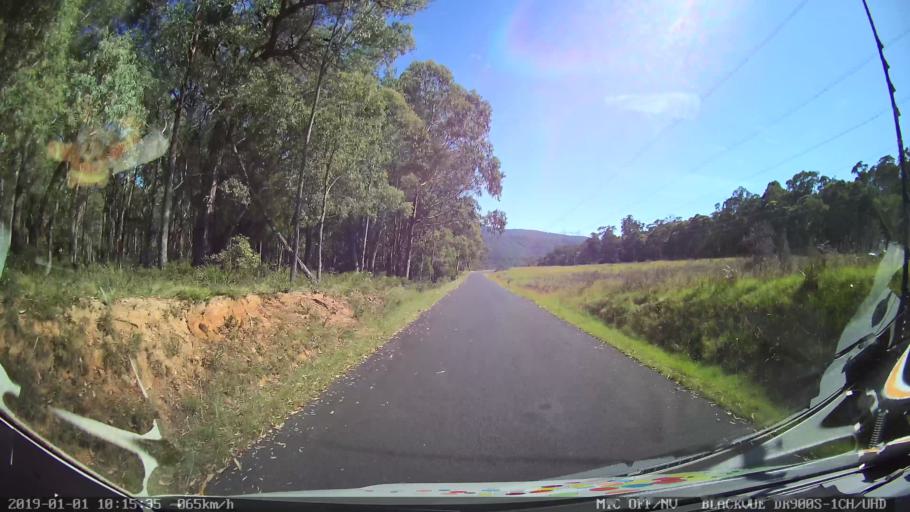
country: AU
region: New South Wales
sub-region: Snowy River
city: Jindabyne
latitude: -36.1002
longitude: 148.1621
